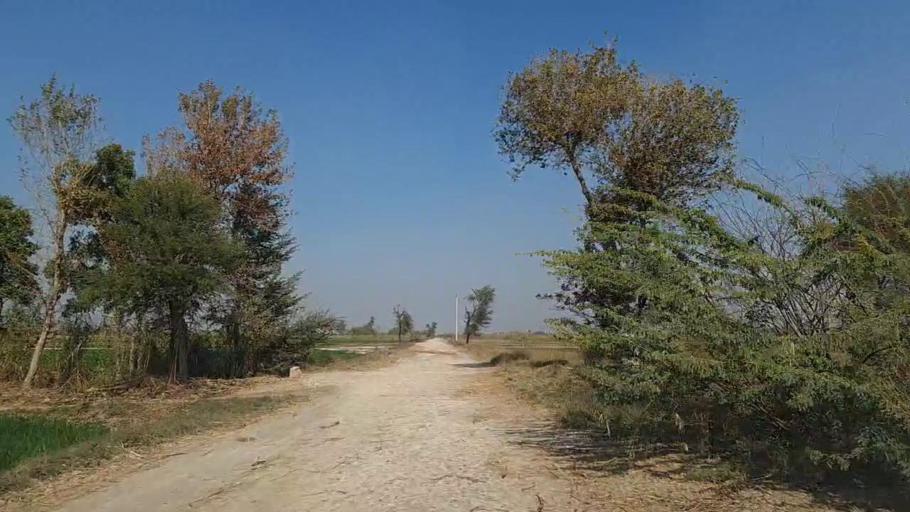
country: PK
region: Sindh
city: Daur
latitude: 26.4887
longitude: 68.3384
